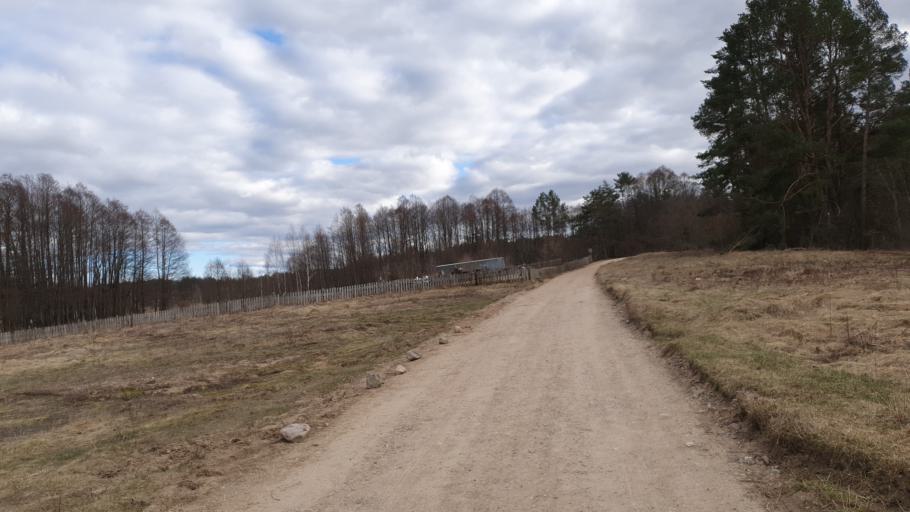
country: LT
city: Grigiskes
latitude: 54.7341
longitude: 25.0272
